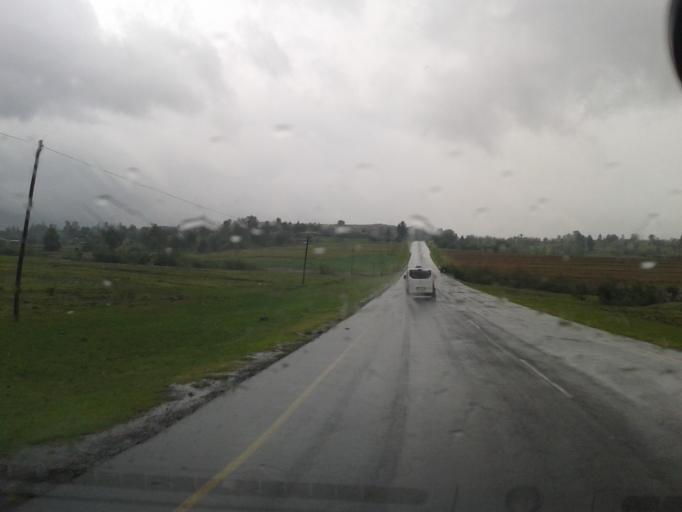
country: LS
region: Maseru
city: Nako
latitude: -29.6361
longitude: 27.4794
